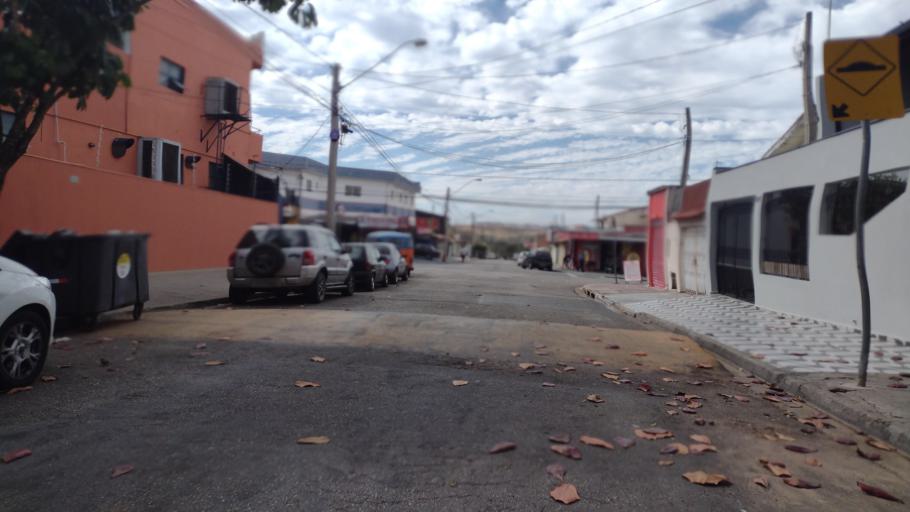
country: BR
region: Sao Paulo
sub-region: Sorocaba
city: Sorocaba
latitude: -23.4312
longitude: -47.4594
